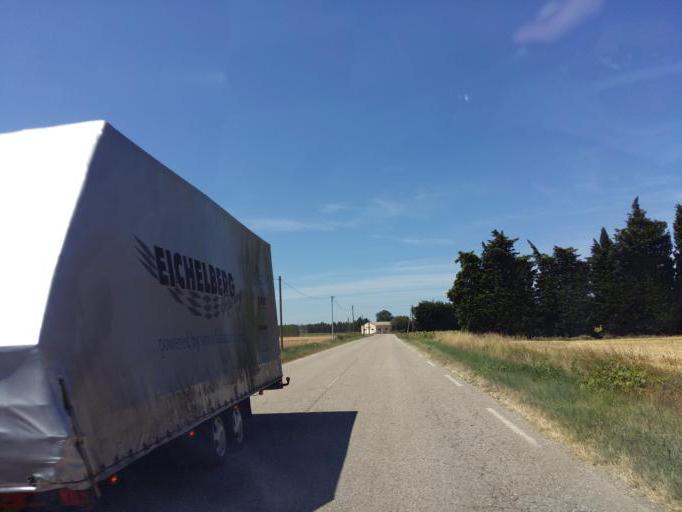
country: FR
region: Provence-Alpes-Cote d'Azur
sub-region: Departement du Vaucluse
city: Mornas
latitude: 44.1865
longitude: 4.7387
